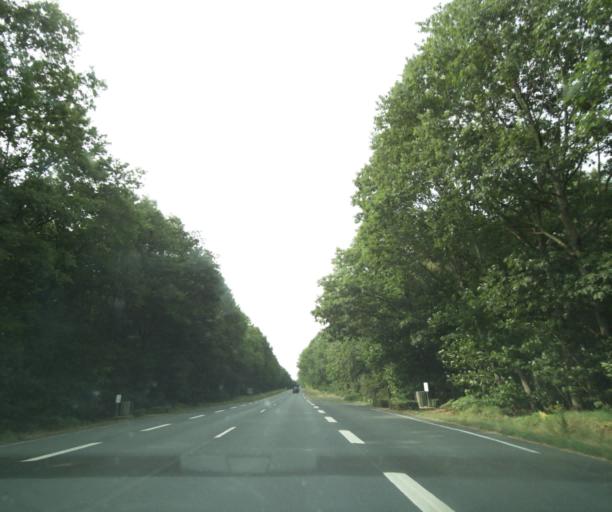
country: FR
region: Pays de la Loire
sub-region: Departement de la Sarthe
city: Marigne-Laille
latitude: 47.7665
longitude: 0.3520
